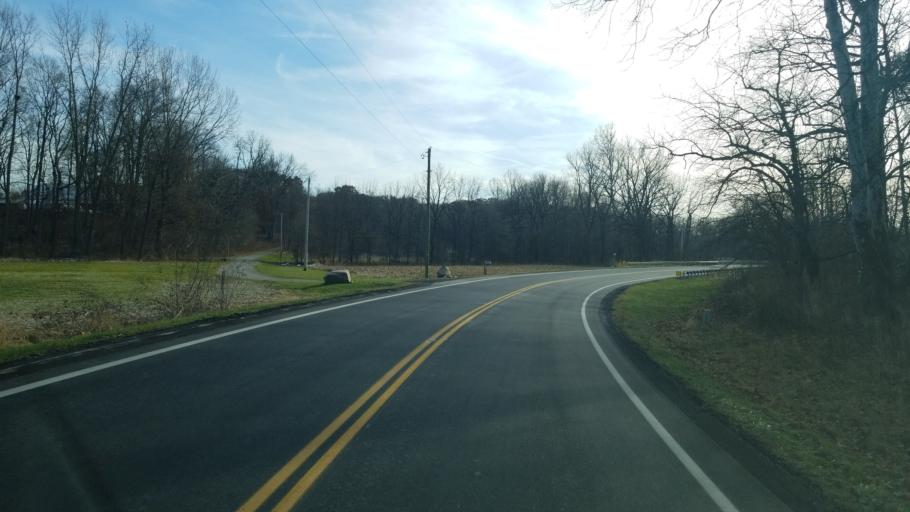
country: US
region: Ohio
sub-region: Ashland County
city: Ashland
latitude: 40.9575
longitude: -82.2576
